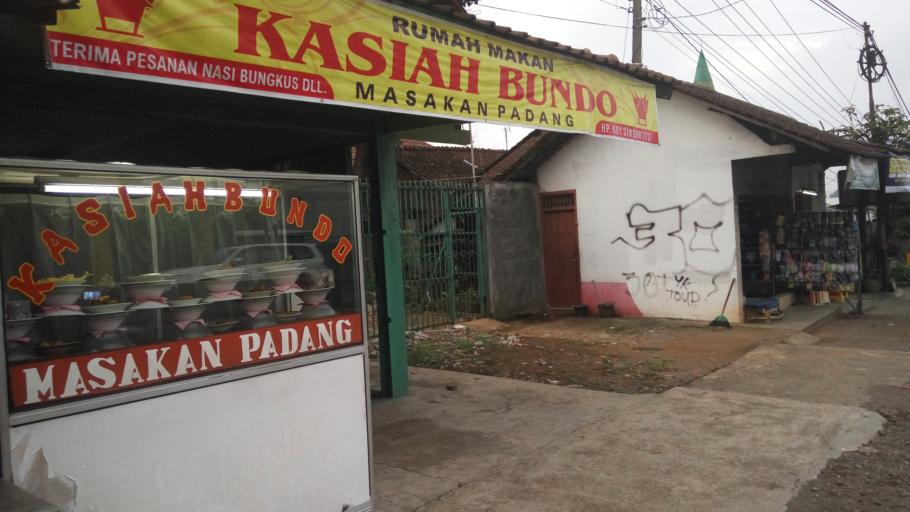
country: ID
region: Central Java
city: Ambarawa
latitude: -7.2267
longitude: 110.4308
